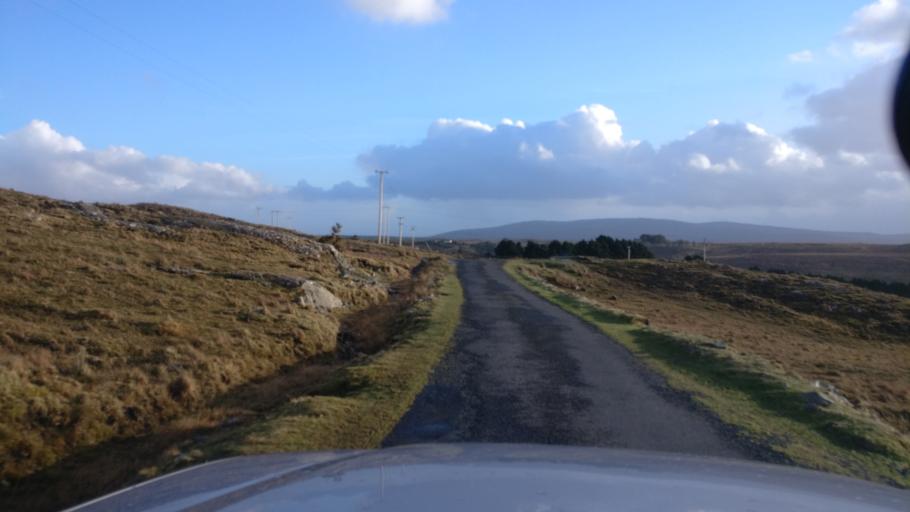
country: IE
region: Connaught
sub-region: County Galway
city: Clifden
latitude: 53.4714
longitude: -9.7278
